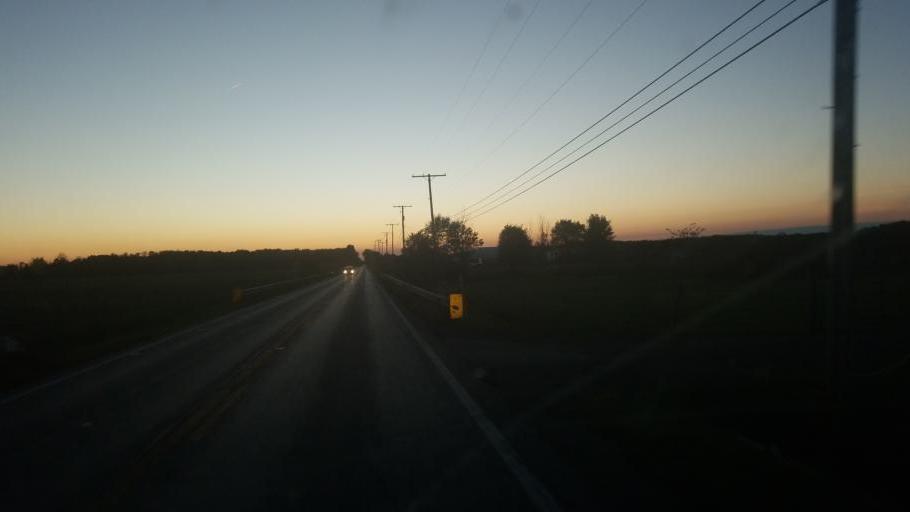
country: US
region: Ohio
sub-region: Ashtabula County
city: Jefferson
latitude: 41.7517
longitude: -80.6693
